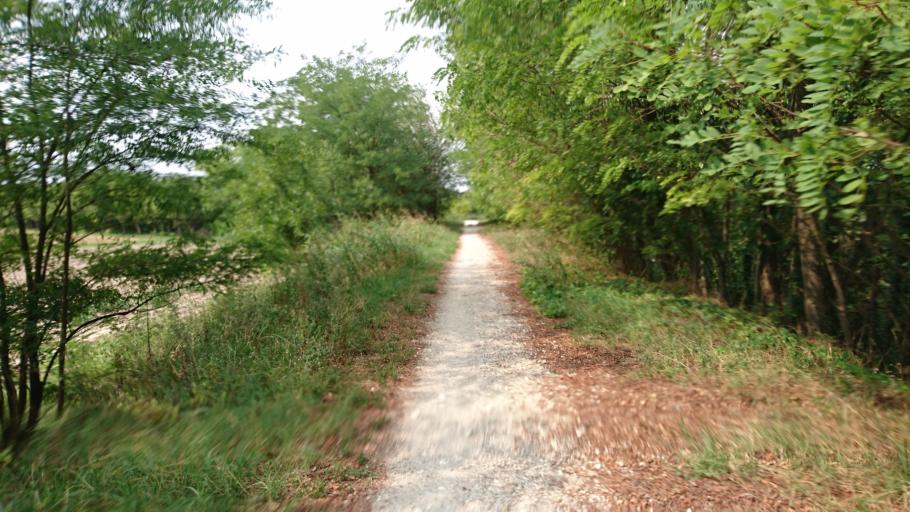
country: IT
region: Veneto
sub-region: Provincia di Padova
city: Saletto
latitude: 45.4703
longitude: 11.8588
